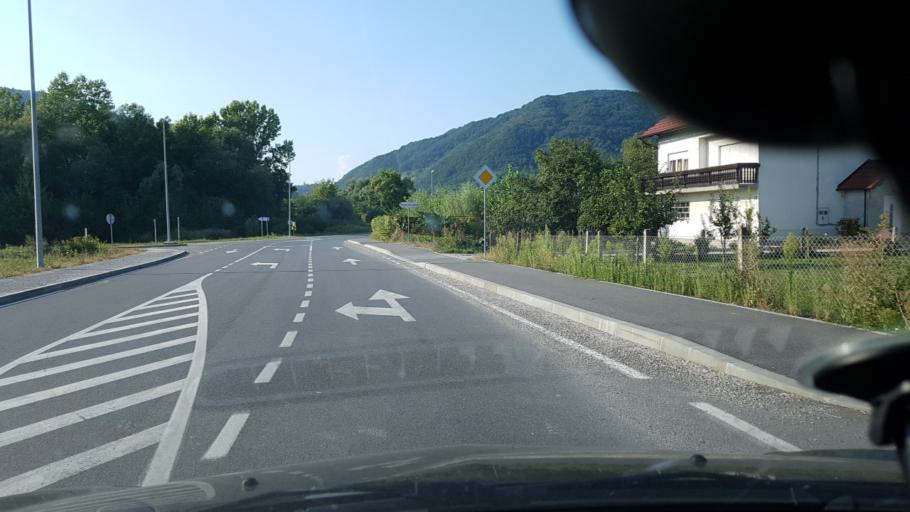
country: SI
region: Bistrica ob Sotli
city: Bistrica ob Sotli
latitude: 46.0393
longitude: 15.7328
